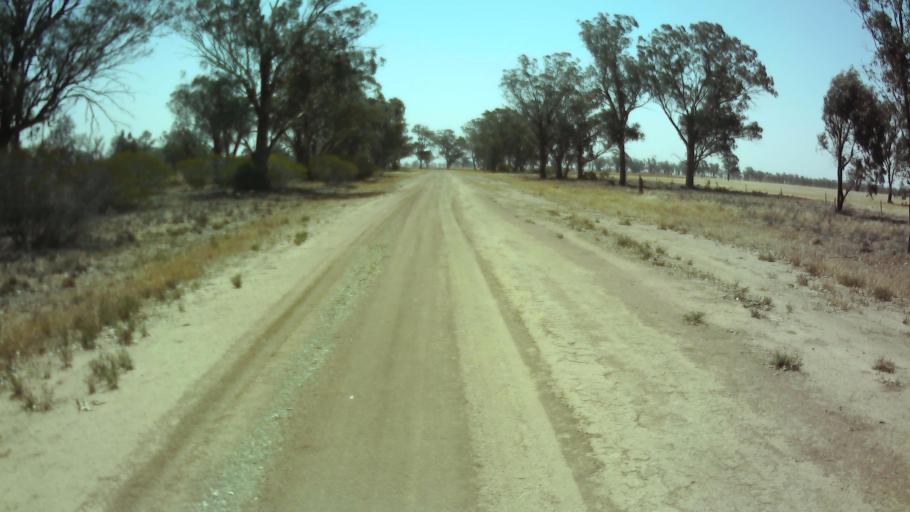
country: AU
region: New South Wales
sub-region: Weddin
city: Grenfell
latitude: -33.9377
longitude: 147.8082
